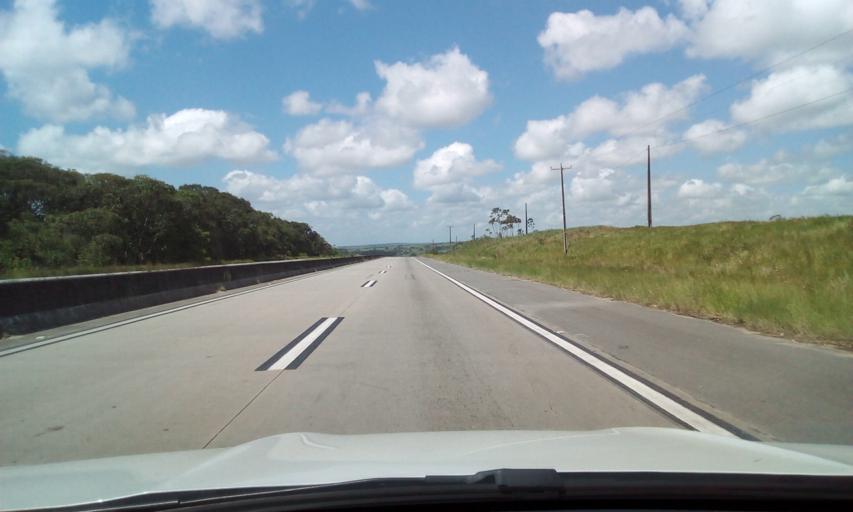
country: BR
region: Paraiba
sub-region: Alhandra
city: Alhandra
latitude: -7.4473
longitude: -34.9791
